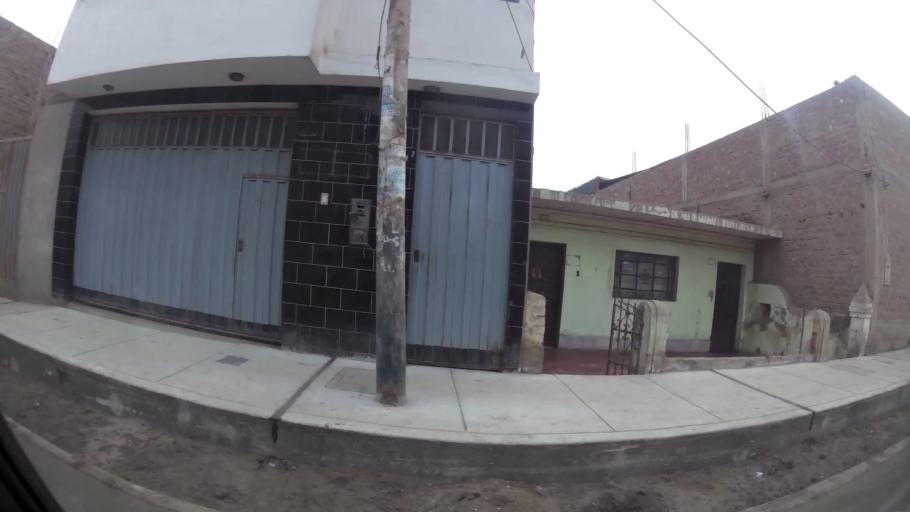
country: PE
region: Lima
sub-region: Provincia de Huaral
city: Huaral
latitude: -11.4967
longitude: -77.2003
